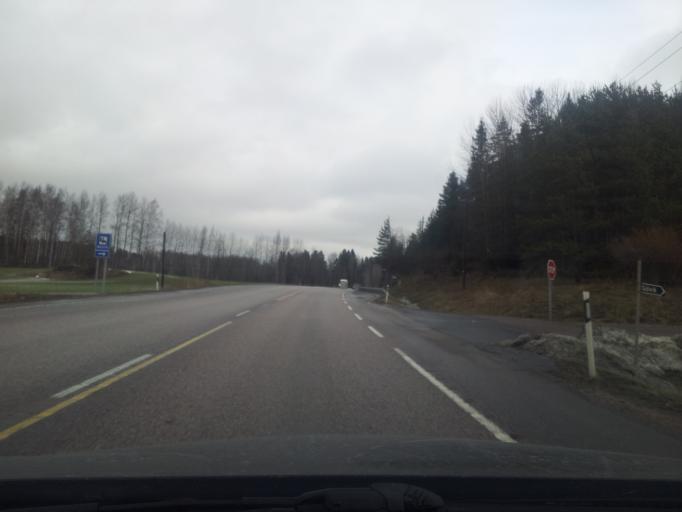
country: FI
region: Uusimaa
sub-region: Helsinki
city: Espoo
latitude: 60.1683
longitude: 24.5488
